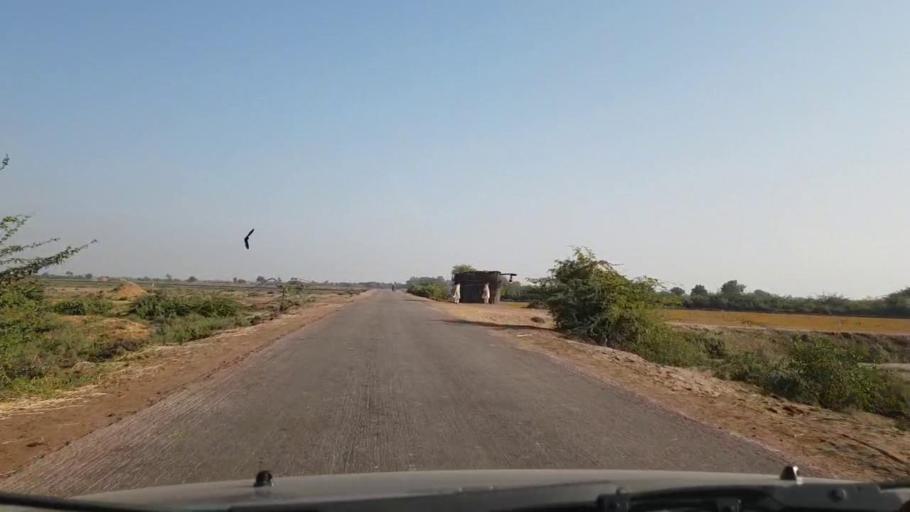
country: PK
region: Sindh
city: Tando Bago
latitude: 24.8690
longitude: 69.0546
